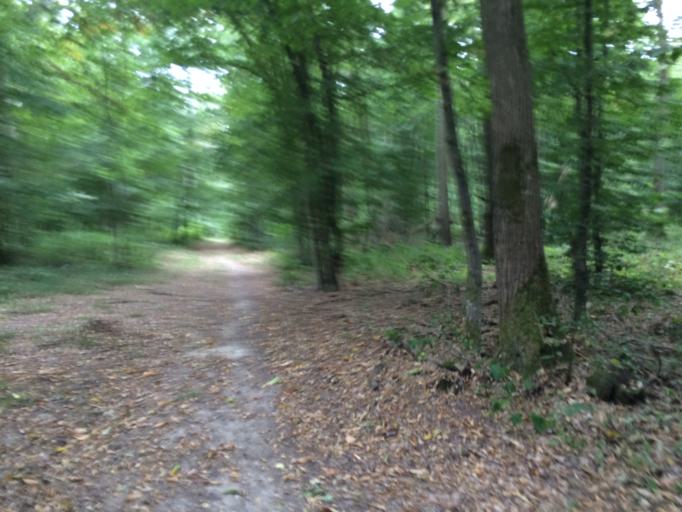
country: FR
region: Ile-de-France
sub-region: Departement de l'Essonne
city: Quincy-sous-Senart
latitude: 48.6539
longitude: 2.5335
